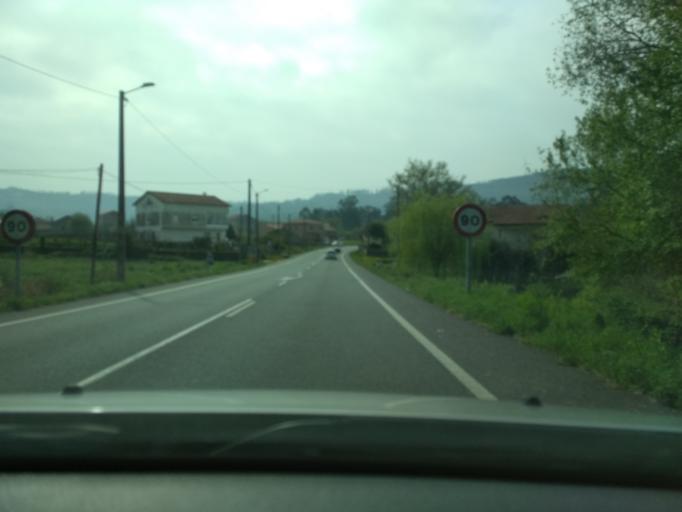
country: ES
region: Galicia
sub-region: Provincia de Pontevedra
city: Catoira
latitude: 42.6699
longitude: -8.7066
